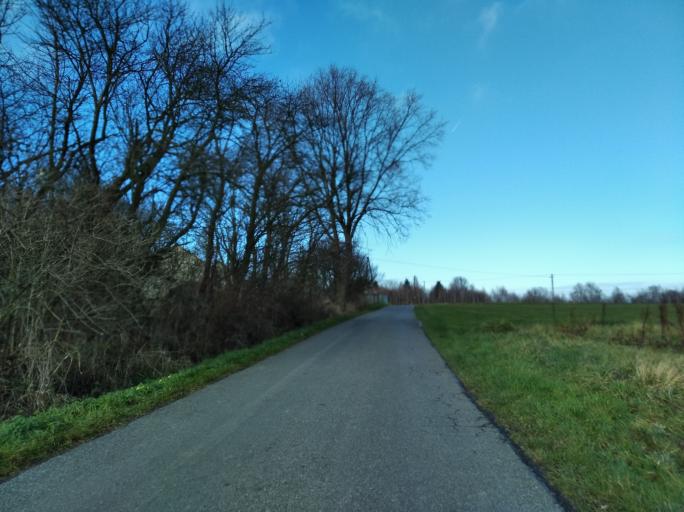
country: PL
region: Subcarpathian Voivodeship
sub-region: Powiat strzyzowski
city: Babica
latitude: 49.9133
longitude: 21.8466
